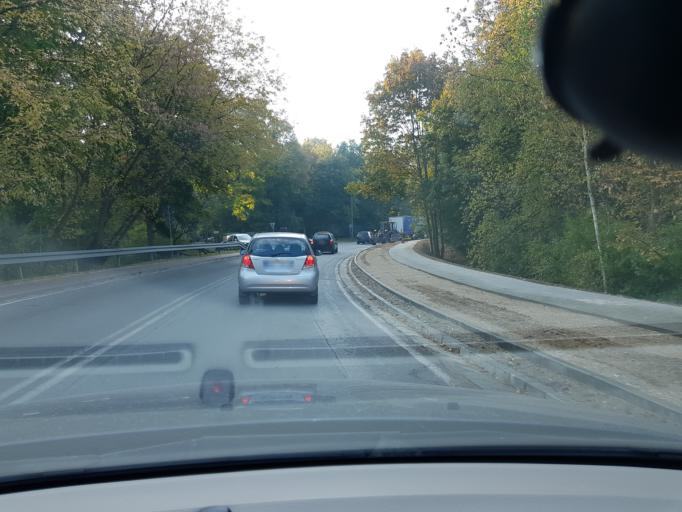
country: PL
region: Masovian Voivodeship
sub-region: Powiat otwocki
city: Jozefow
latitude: 52.1749
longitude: 21.2940
